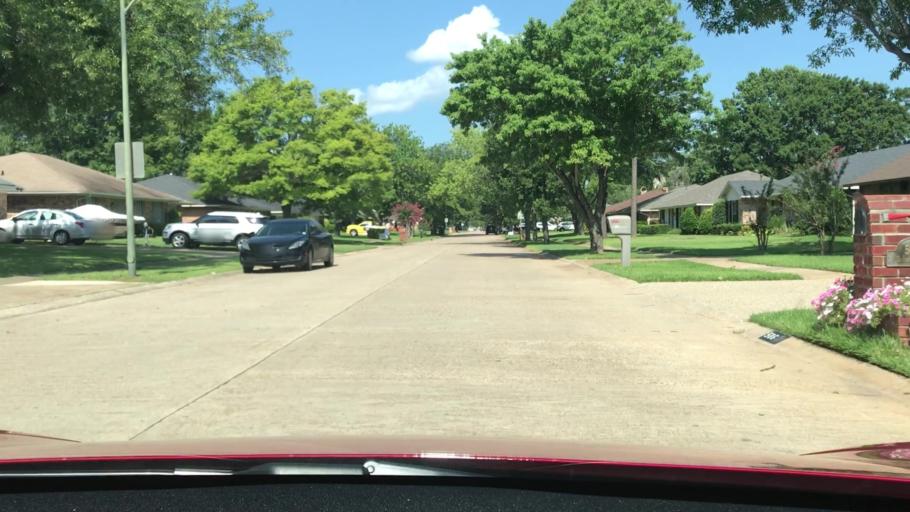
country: US
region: Louisiana
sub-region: Bossier Parish
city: Bossier City
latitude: 32.4197
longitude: -93.7093
